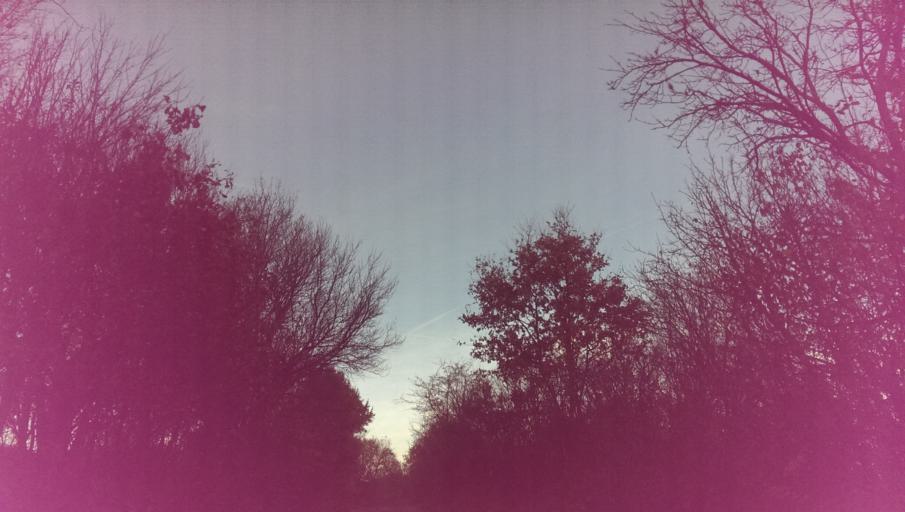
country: CZ
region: Zlin
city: Brezolupy
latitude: 49.1410
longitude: 17.6040
